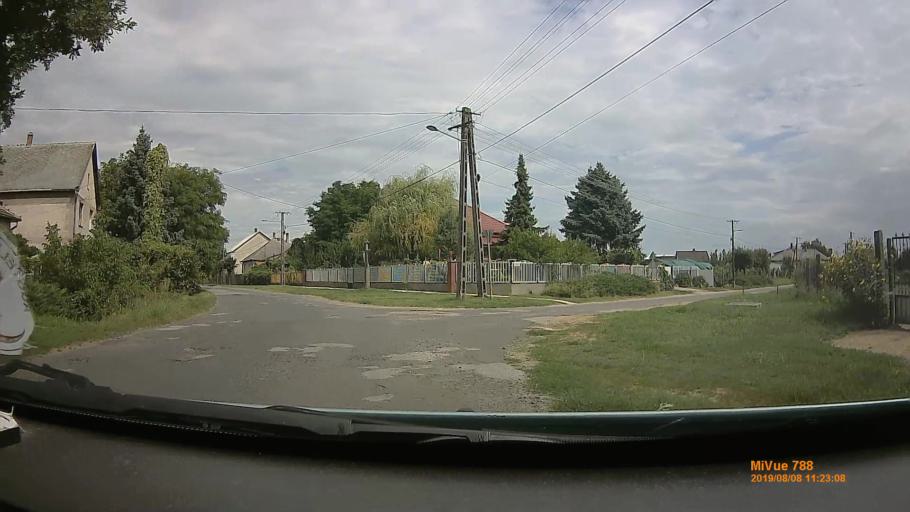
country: HU
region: Szabolcs-Szatmar-Bereg
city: Balkany
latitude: 47.7660
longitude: 21.8501
